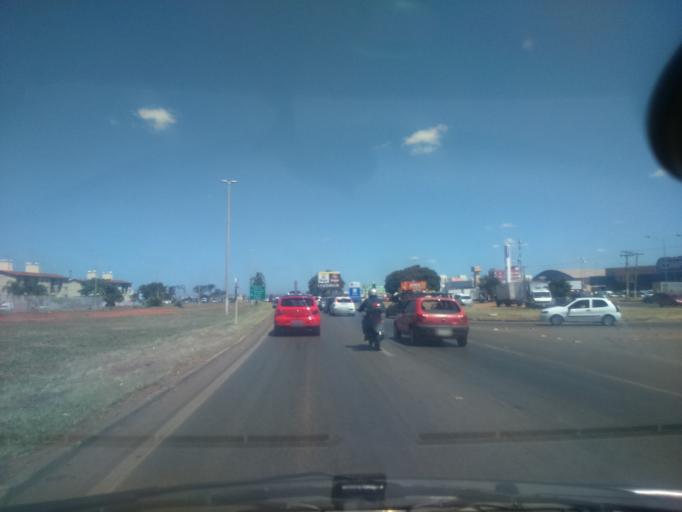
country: BR
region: Goias
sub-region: Luziania
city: Luziania
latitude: -16.0714
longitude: -47.9852
